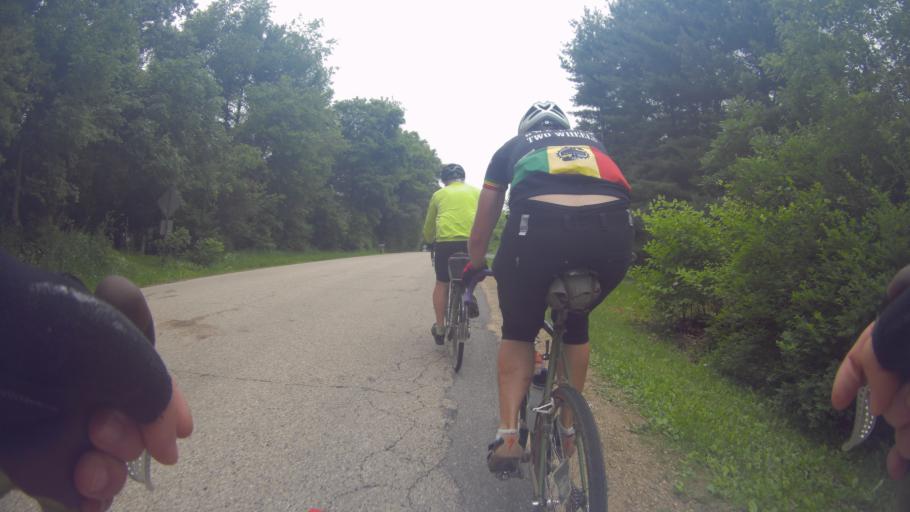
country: US
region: Wisconsin
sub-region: Green County
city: Brooklyn
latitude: 42.8804
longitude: -89.3888
